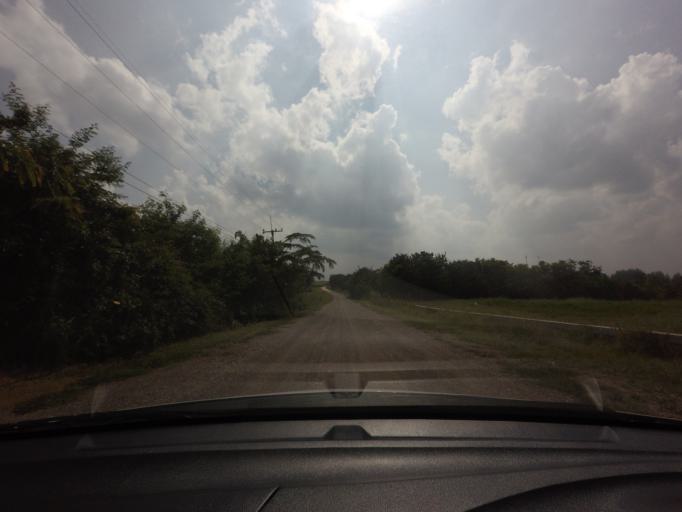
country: TH
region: Nakhon Ratchasima
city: Pak Chong
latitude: 14.5365
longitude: 101.5919
